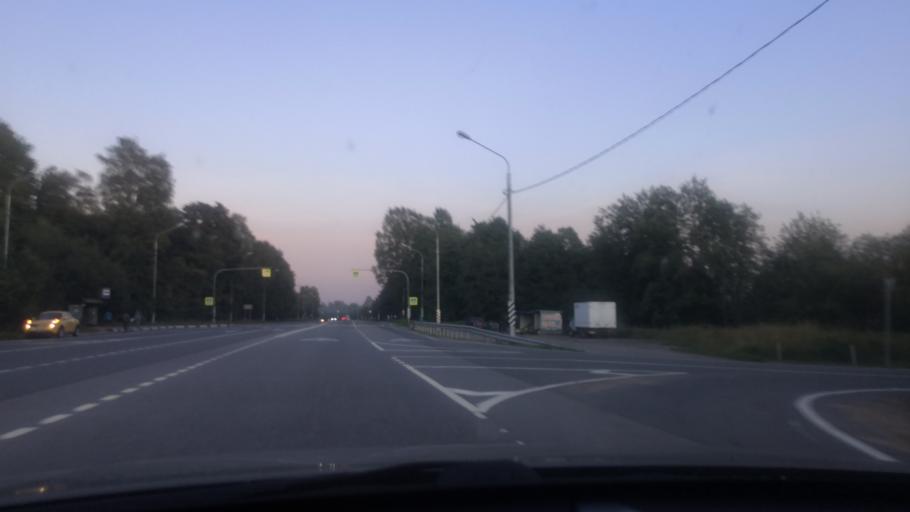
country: RU
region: St.-Petersburg
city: Beloostrov
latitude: 60.1978
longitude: 30.0292
